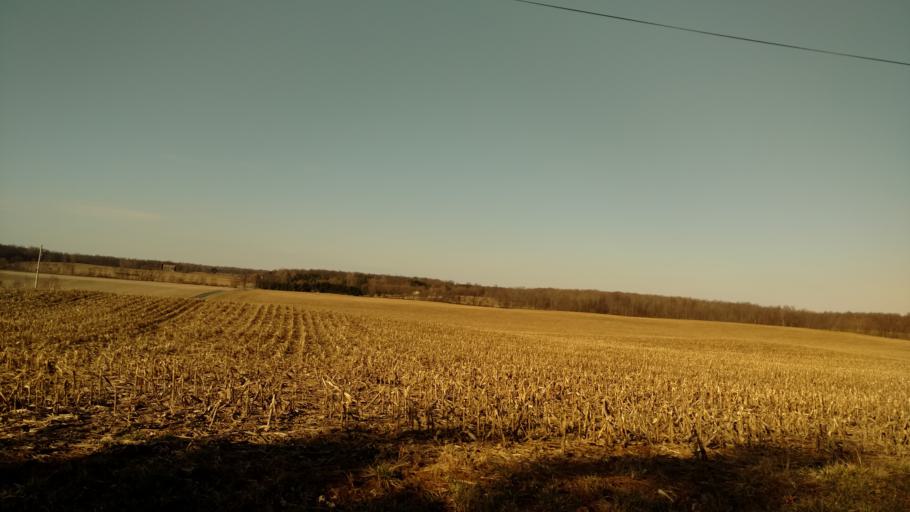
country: US
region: Ohio
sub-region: Crawford County
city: Galion
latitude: 40.7112
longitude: -82.7220
